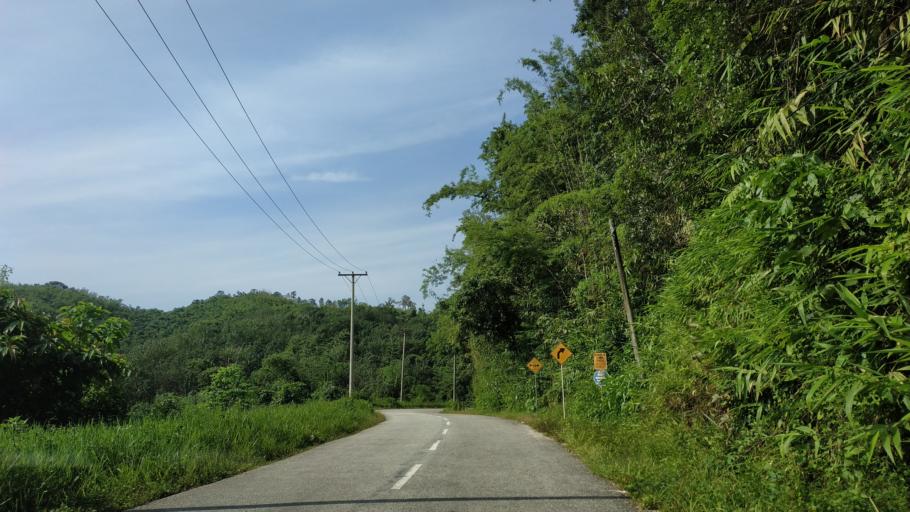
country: TH
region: Kanchanaburi
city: Thong Pha Phum
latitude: 14.6273
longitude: 98.1310
